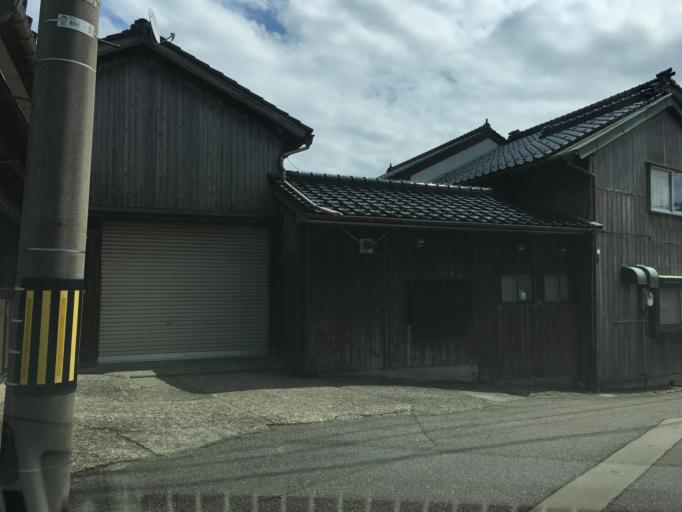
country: JP
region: Toyama
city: Kuragaki-kosugi
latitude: 36.7722
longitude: 137.1252
